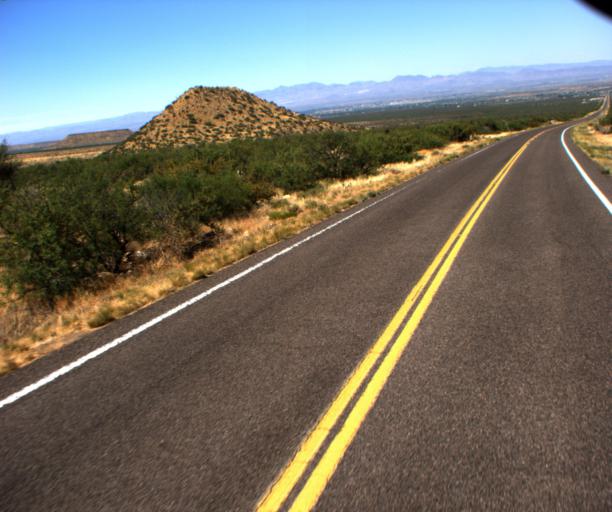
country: US
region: Arizona
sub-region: Graham County
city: Swift Trail Junction
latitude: 32.6893
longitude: -109.7548
